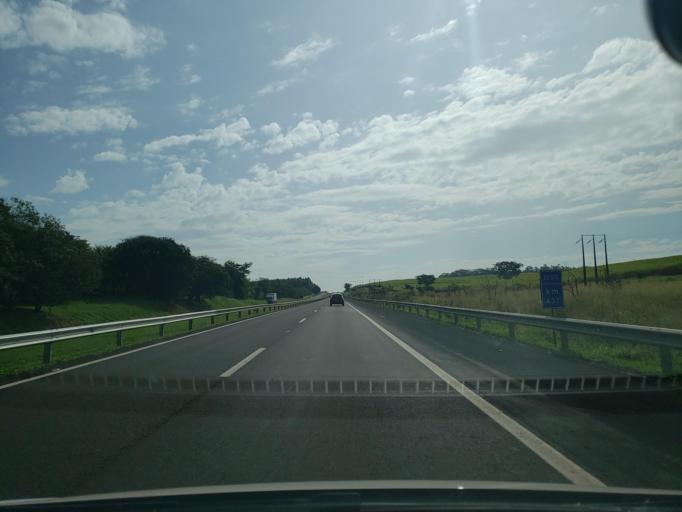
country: BR
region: Sao Paulo
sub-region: Lins
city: Lins
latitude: -21.7291
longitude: -49.7128
